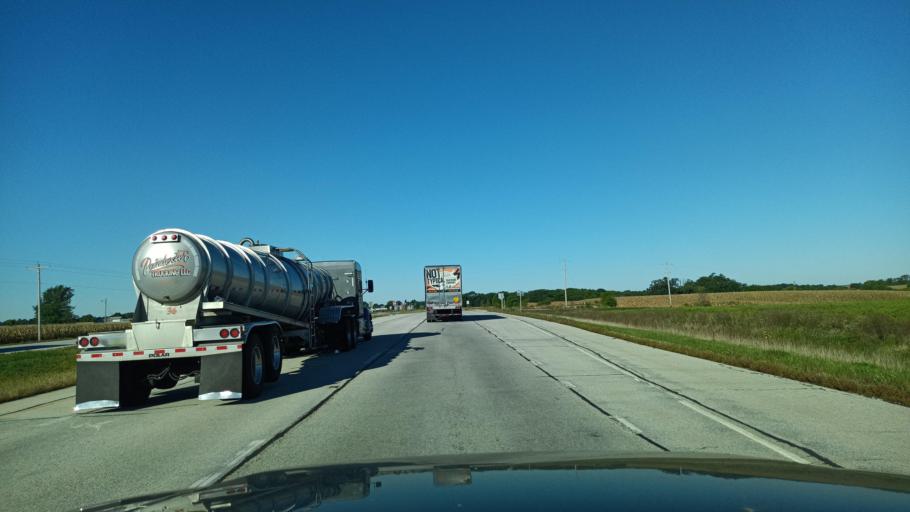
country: US
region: Illinois
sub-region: Henderson County
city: Oquawka
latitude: 40.8512
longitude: -90.8341
